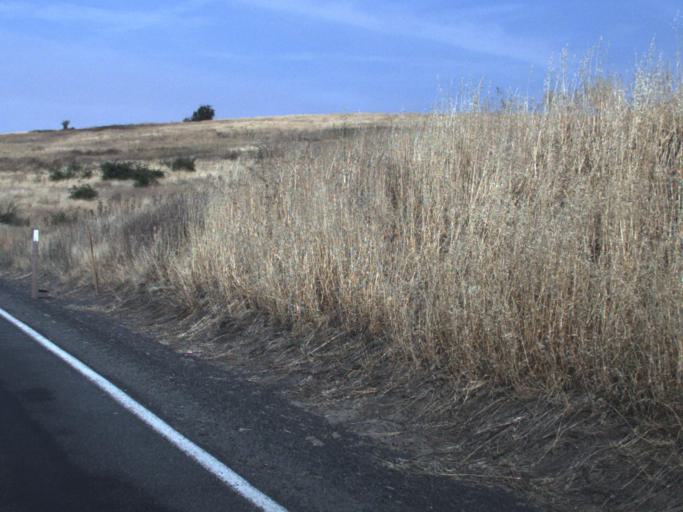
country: US
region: Idaho
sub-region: Benewah County
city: Plummer
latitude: 47.2394
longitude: -117.1202
